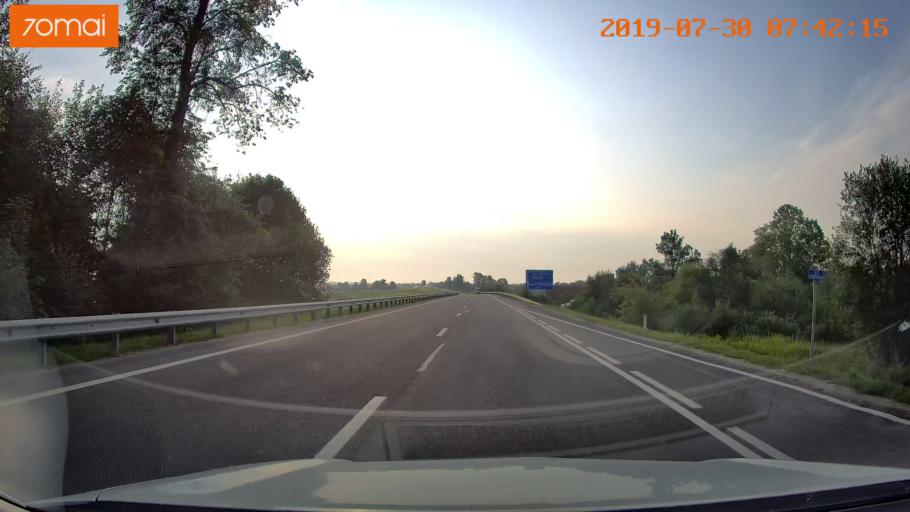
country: RU
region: Kaliningrad
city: Gvardeysk
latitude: 54.6476
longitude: 21.2739
